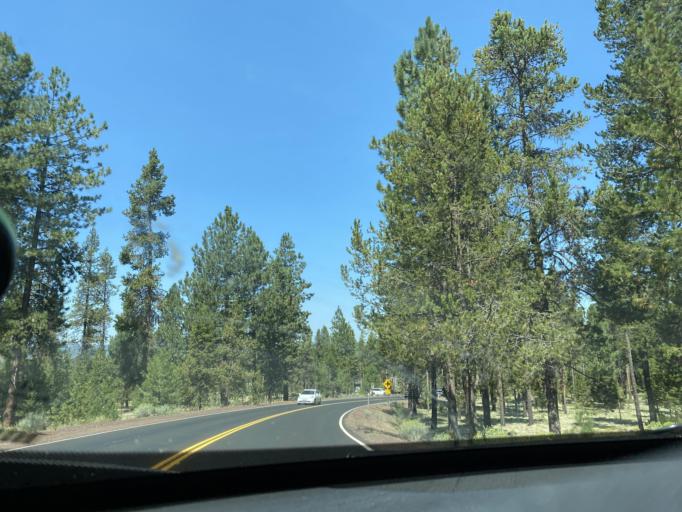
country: US
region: Oregon
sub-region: Deschutes County
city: Sunriver
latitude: 43.8940
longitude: -121.4165
